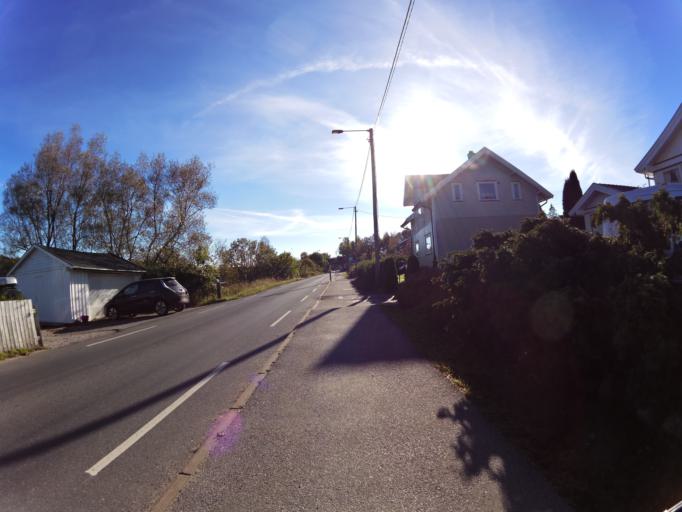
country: NO
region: Ostfold
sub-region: Sarpsborg
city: Sarpsborg
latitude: 59.2709
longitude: 11.0213
